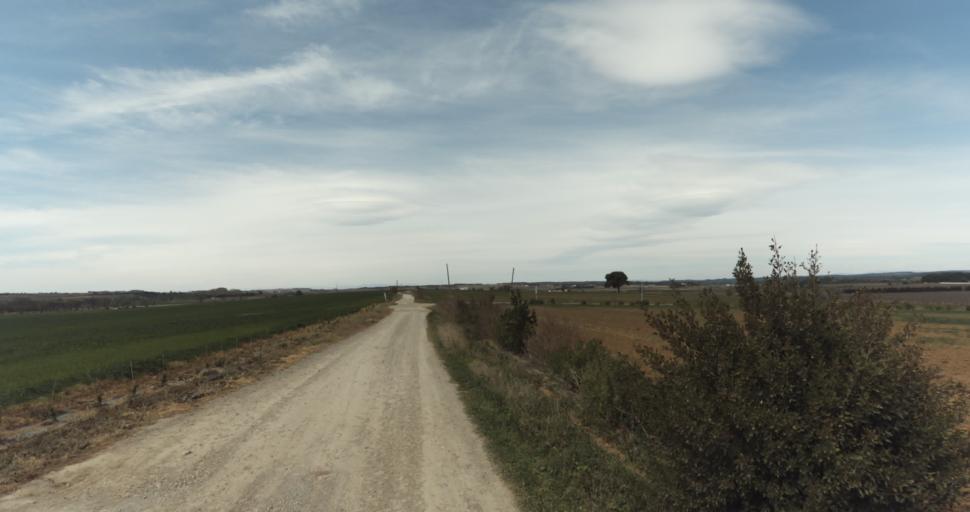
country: FR
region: Languedoc-Roussillon
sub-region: Departement de l'Herault
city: Pinet
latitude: 43.4013
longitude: 3.5598
